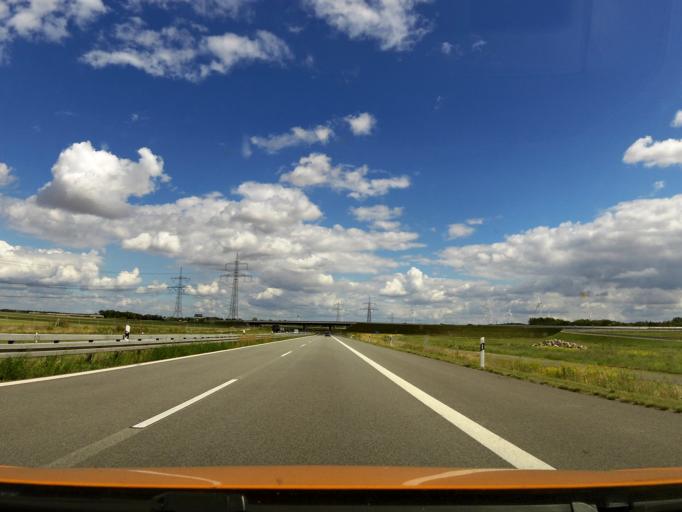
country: DE
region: Brandenburg
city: Ahrensfelde
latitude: 52.6164
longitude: 13.5544
